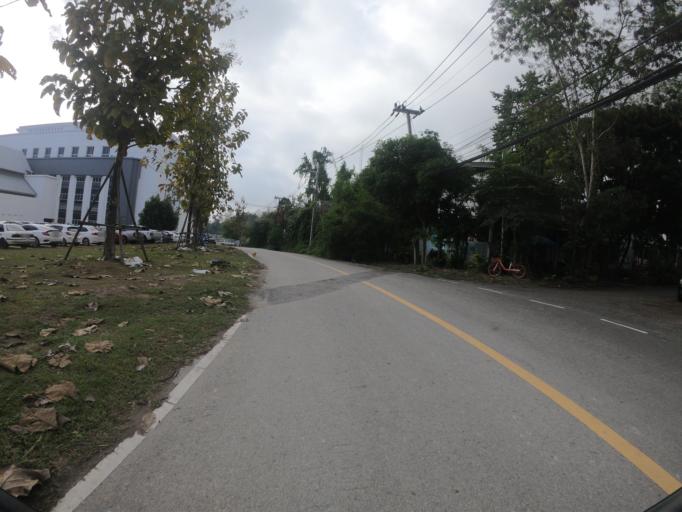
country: TH
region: Chiang Mai
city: Chiang Mai
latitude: 18.8053
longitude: 98.9476
